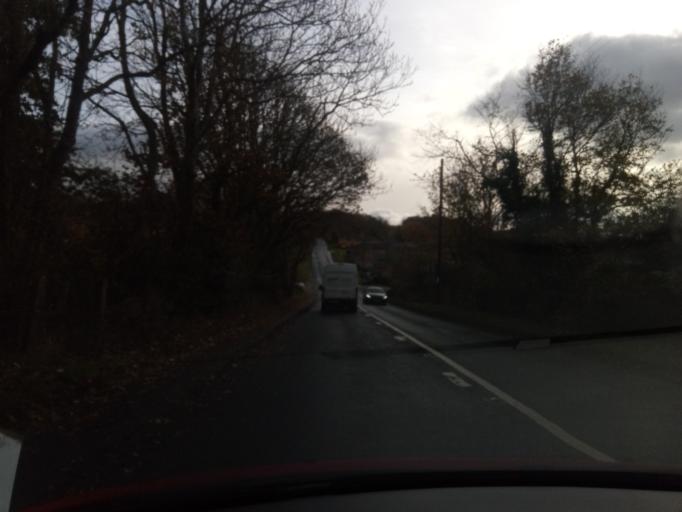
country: GB
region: England
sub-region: Northumberland
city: Wall
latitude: 55.0278
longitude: -2.1257
